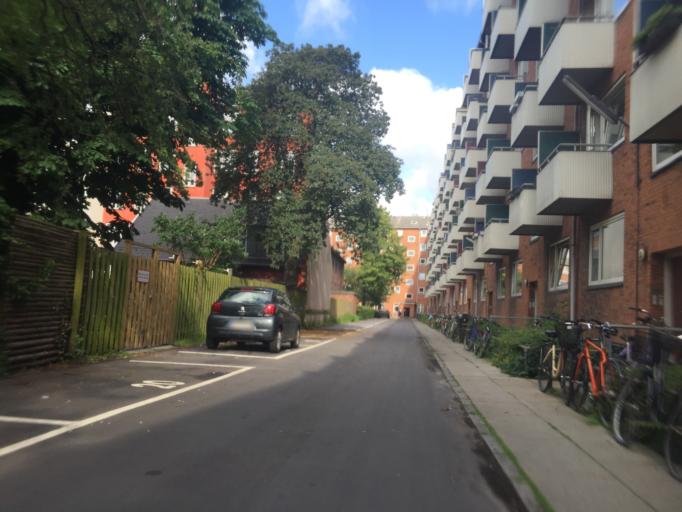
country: DK
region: Capital Region
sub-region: Frederiksberg Kommune
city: Frederiksberg
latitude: 55.6820
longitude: 12.5376
